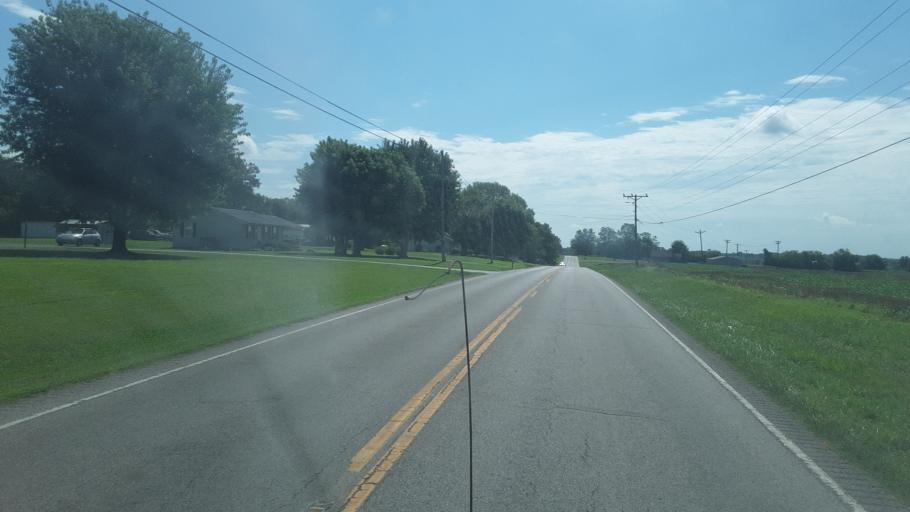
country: US
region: Kentucky
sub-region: Todd County
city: Elkton
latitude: 36.8173
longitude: -87.1867
